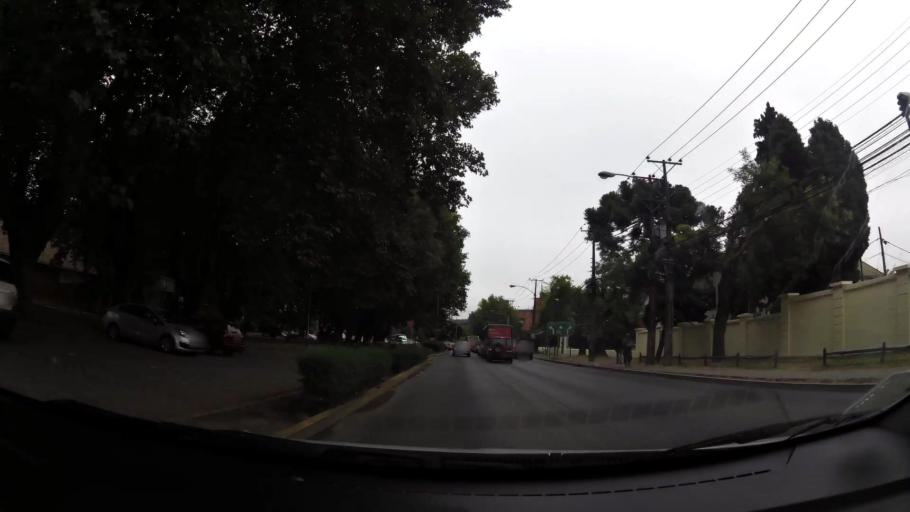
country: CL
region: Biobio
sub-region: Provincia de Concepcion
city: Concepcion
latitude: -36.8149
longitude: -73.0297
